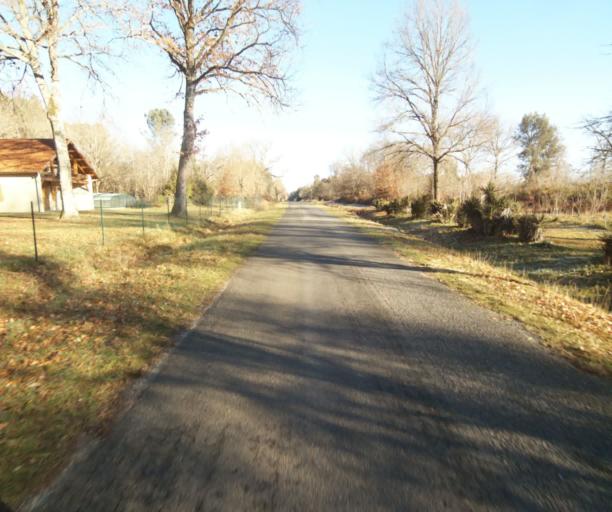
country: FR
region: Aquitaine
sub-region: Departement des Landes
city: Gabarret
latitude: 44.1135
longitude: 0.0811
